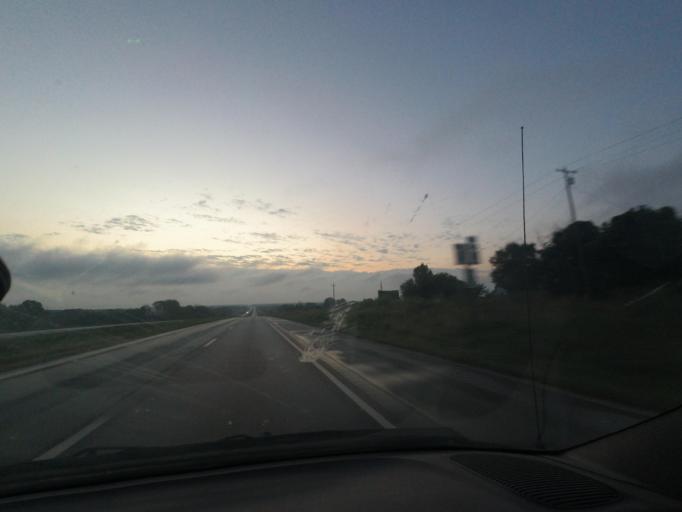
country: US
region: Missouri
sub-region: Linn County
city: Brookfield
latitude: 39.7621
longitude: -93.0075
